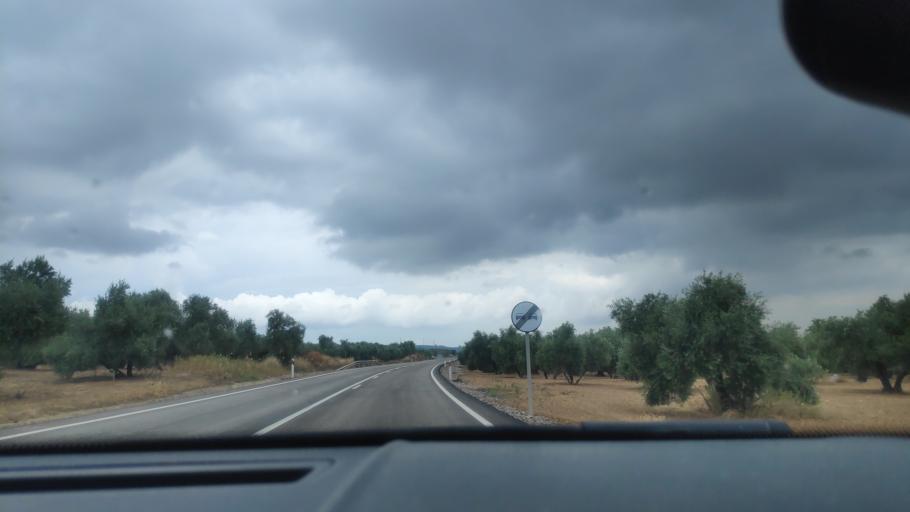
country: ES
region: Andalusia
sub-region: Provincia de Jaen
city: Jabalquinto
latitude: 38.0347
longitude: -3.7581
